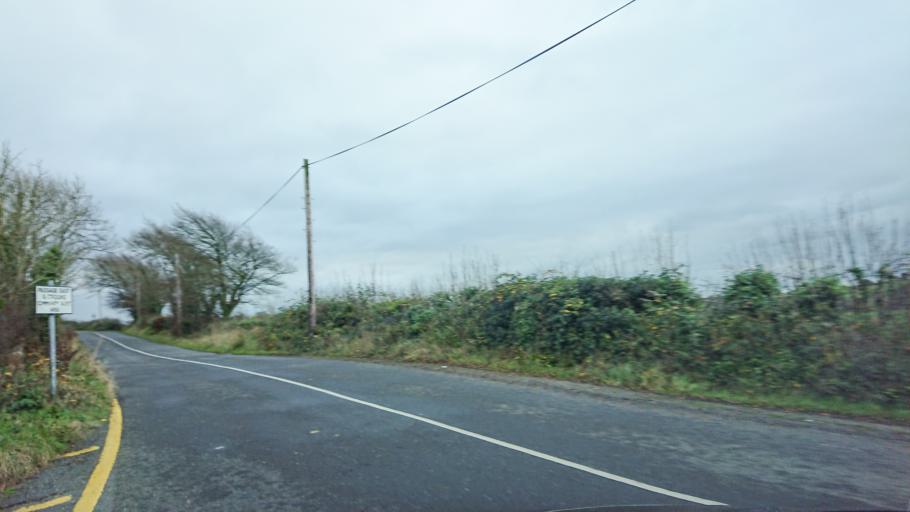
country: IE
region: Munster
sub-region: Waterford
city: Dunmore East
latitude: 52.2419
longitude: -7.0019
